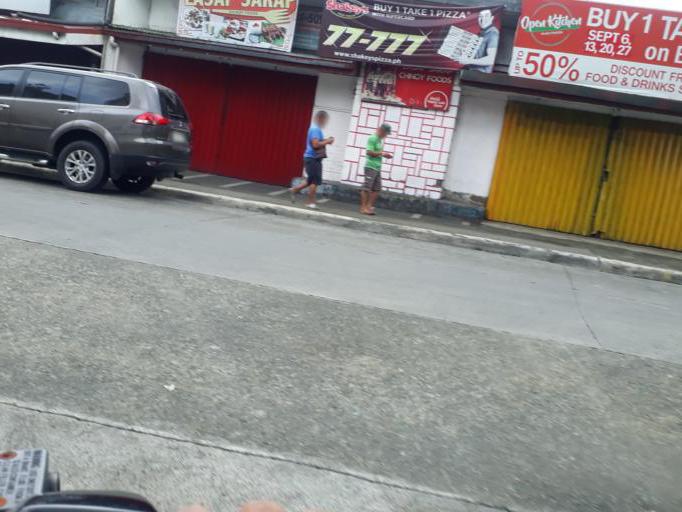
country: PH
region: Metro Manila
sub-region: San Juan
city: San Juan
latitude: 14.6220
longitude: 121.0437
